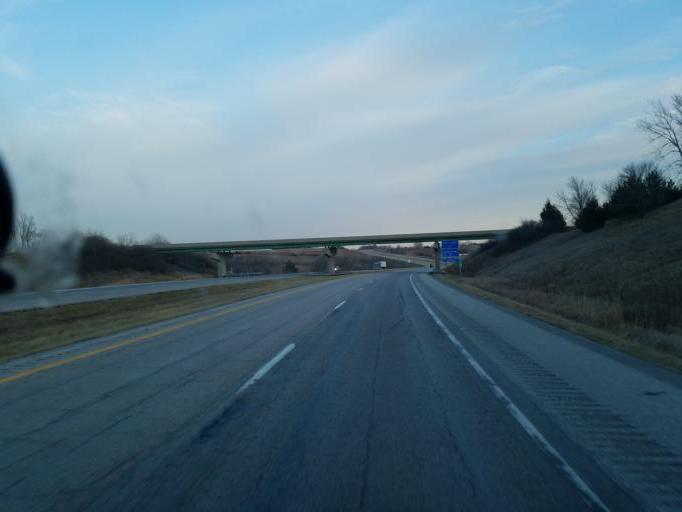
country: US
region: Iowa
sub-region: Harrison County
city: Missouri Valley
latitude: 41.4946
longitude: -95.8627
